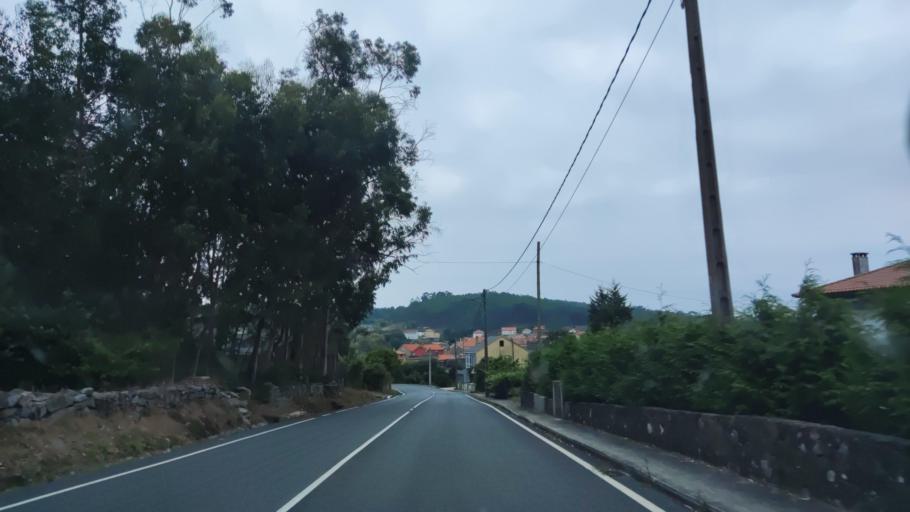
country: ES
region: Galicia
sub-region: Provincia de Pontevedra
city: Catoira
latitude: 42.6644
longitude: -8.7449
